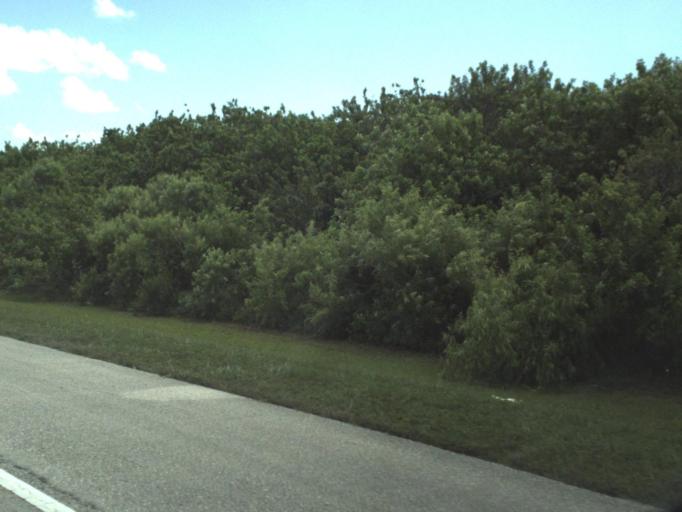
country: US
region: Florida
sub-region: Brevard County
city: Cape Canaveral
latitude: 28.4056
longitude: -80.6236
